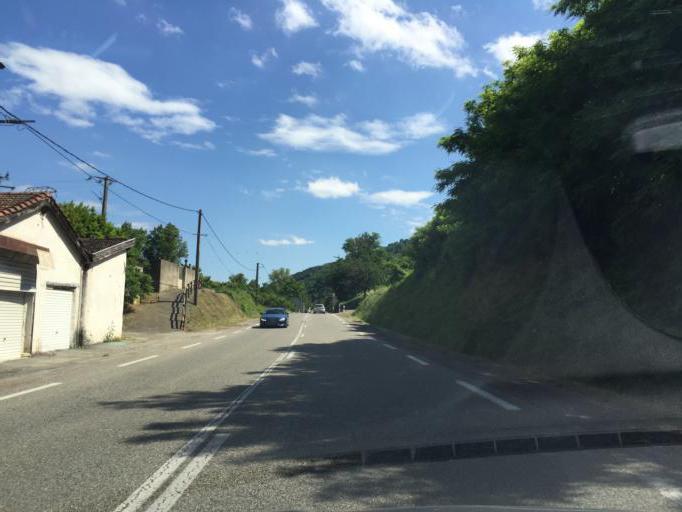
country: FR
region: Rhone-Alpes
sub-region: Departement de la Drome
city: Saint-Vallier
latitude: 45.1728
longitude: 4.8045
